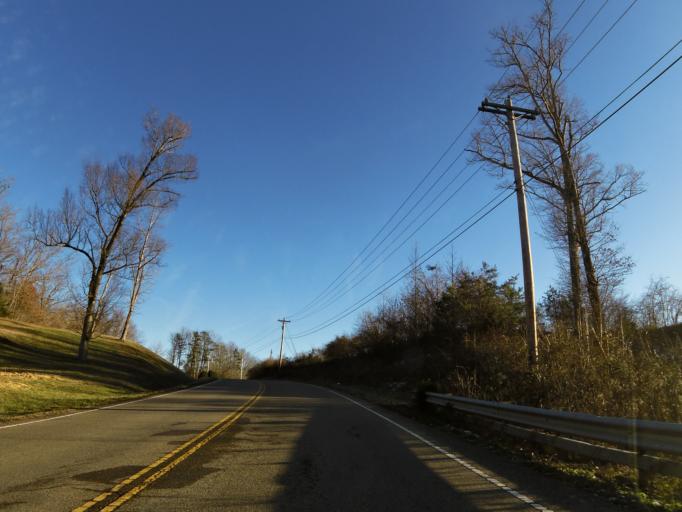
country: US
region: Tennessee
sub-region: Knox County
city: Farragut
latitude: 35.8816
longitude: -84.0951
